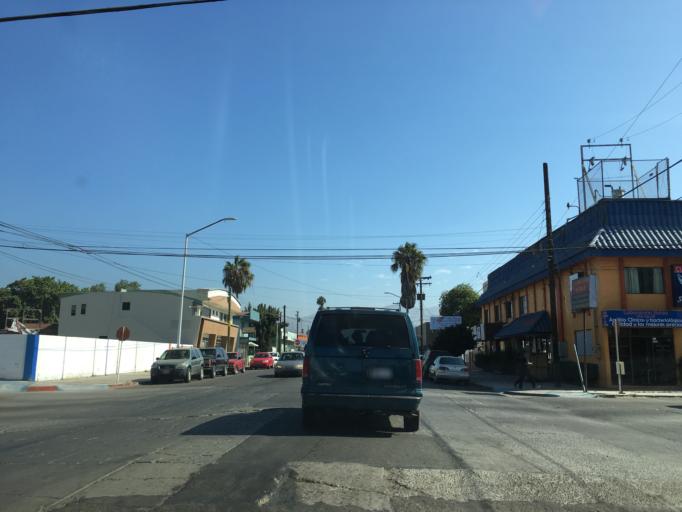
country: MX
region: Baja California
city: Ensenada
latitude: 31.8629
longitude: -116.6166
